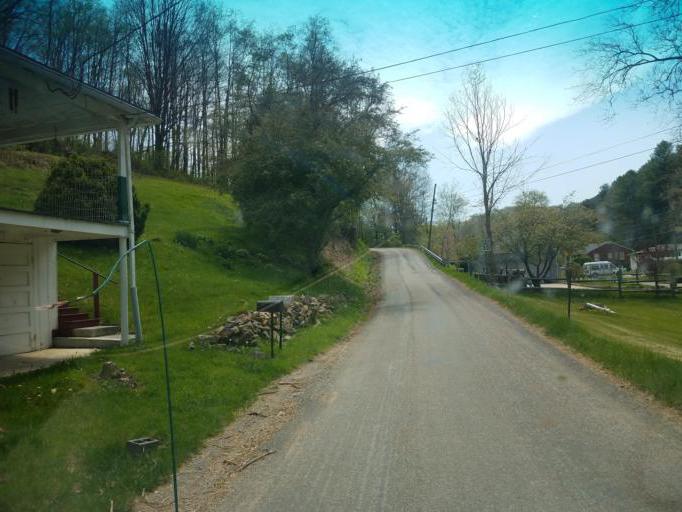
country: US
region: Virginia
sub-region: Smyth County
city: Marion
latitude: 36.8085
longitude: -81.4659
